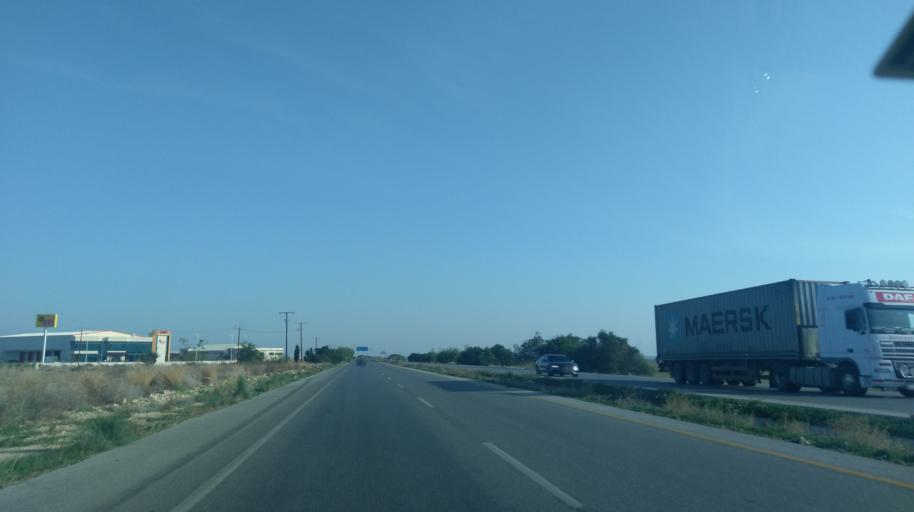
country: CY
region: Ammochostos
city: Acheritou
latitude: 35.1572
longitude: 33.8397
